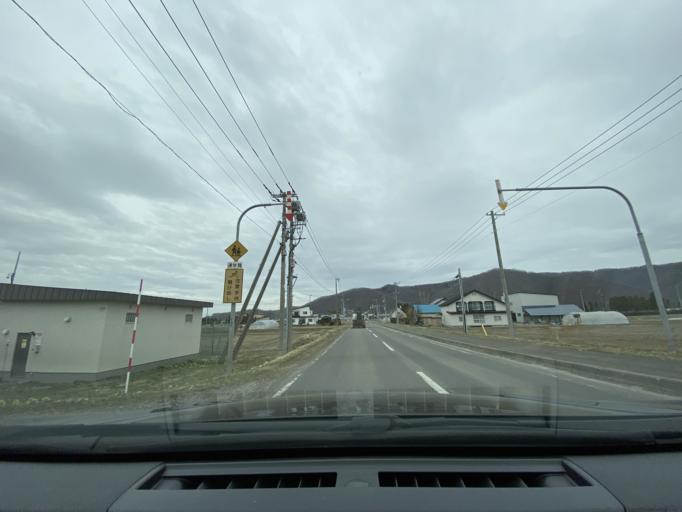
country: JP
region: Hokkaido
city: Nayoro
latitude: 44.1298
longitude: 142.4850
